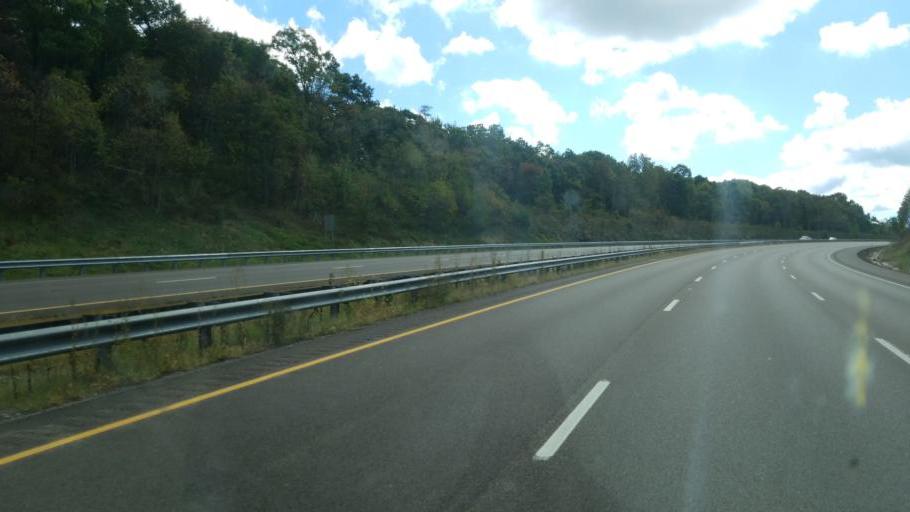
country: US
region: Pennsylvania
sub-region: Somerset County
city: Meyersdale
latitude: 39.6898
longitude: -79.1889
